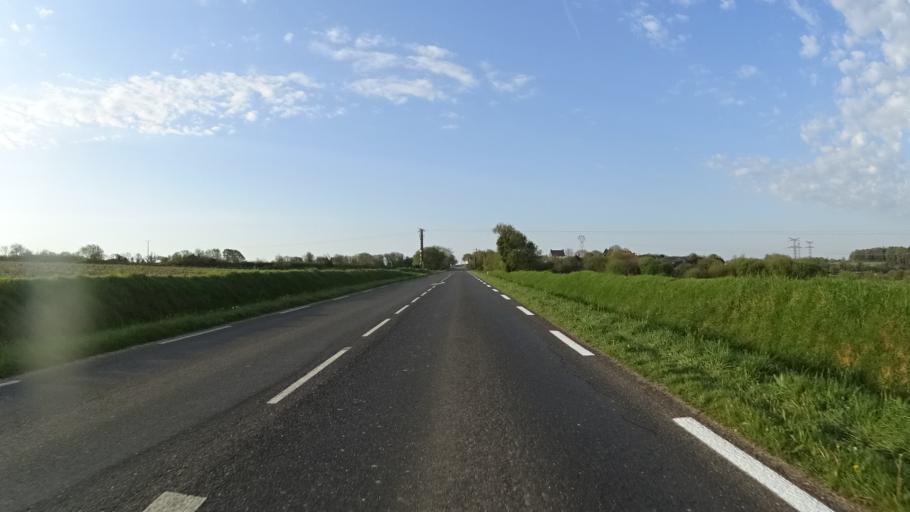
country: FR
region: Brittany
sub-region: Departement du Finistere
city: La Roche-Maurice
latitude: 48.4438
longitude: -4.1836
